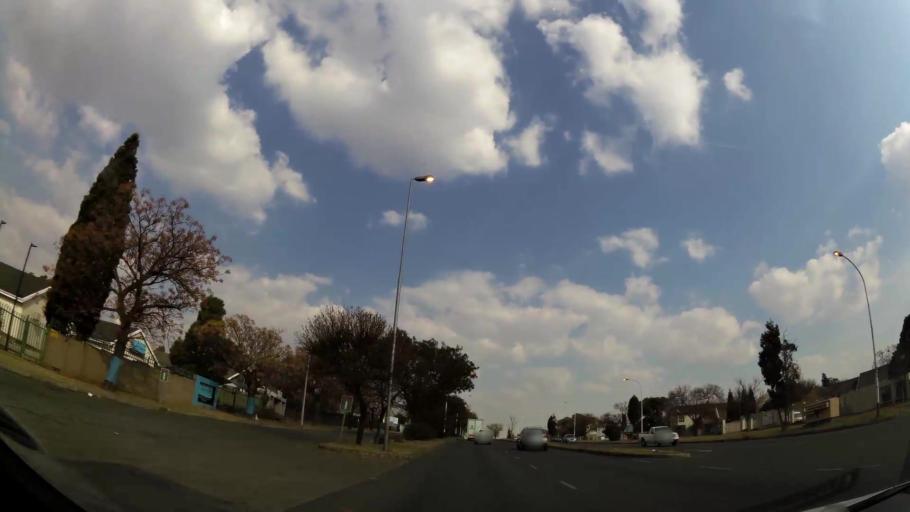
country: ZA
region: Gauteng
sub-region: Ekurhuleni Metropolitan Municipality
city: Boksburg
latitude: -26.2436
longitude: 28.2464
